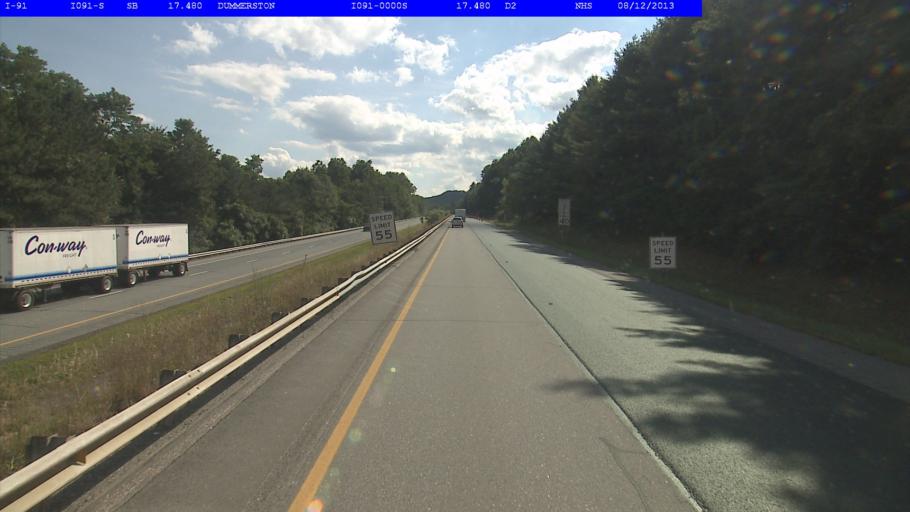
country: US
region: New Hampshire
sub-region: Cheshire County
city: Westmoreland
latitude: 42.9590
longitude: -72.5307
